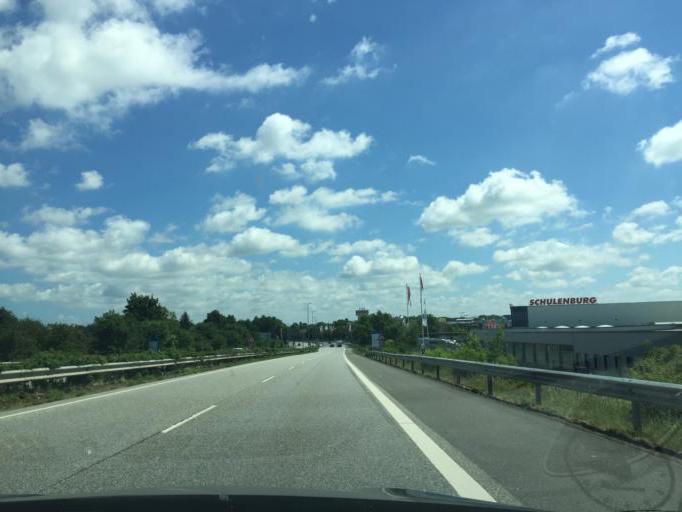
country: DE
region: Schleswig-Holstein
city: Harrislee
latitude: 54.7764
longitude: 9.3903
